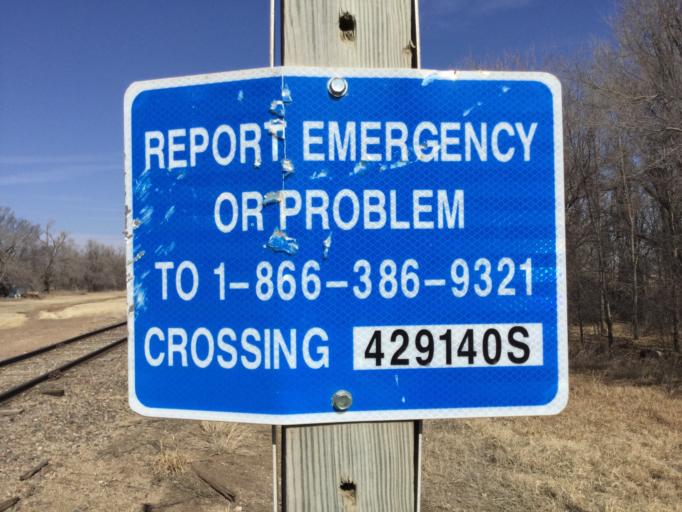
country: US
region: Kansas
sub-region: Rice County
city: Lyons
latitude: 38.3405
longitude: -98.1927
